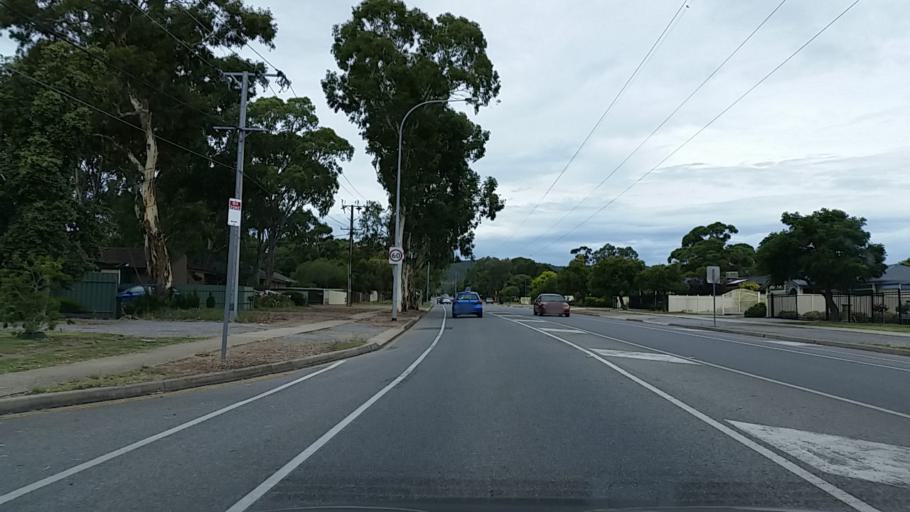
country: AU
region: South Australia
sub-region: Tea Tree Gully
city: Hope Valley
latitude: -34.8327
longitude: 138.7010
